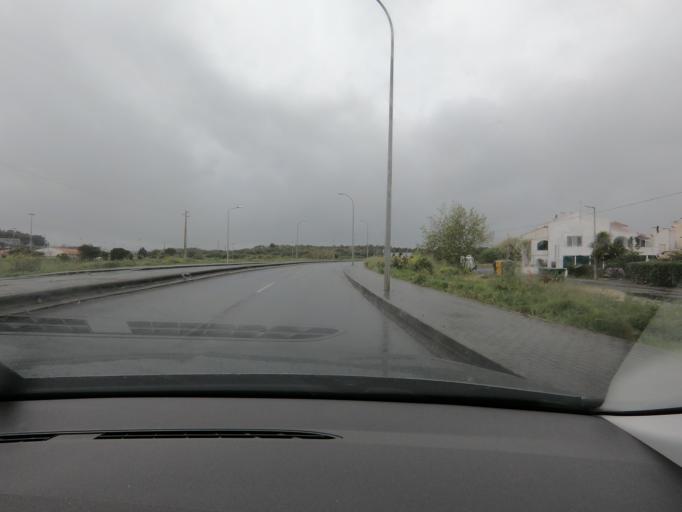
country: PT
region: Lisbon
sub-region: Sintra
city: Sintra
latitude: 38.8010
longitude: -9.3543
